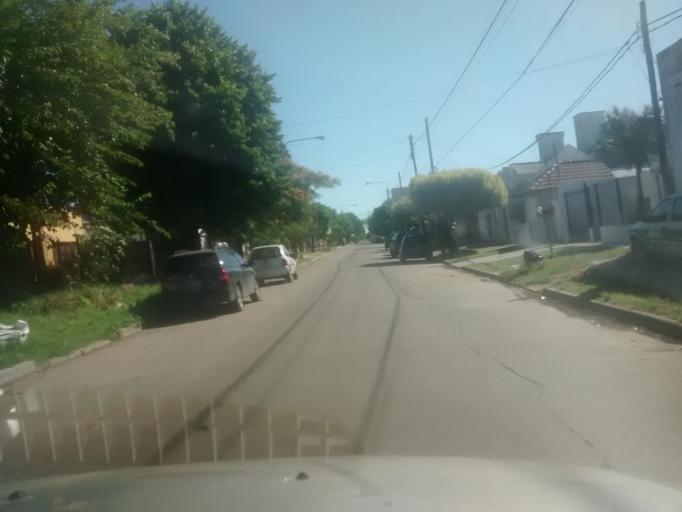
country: AR
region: Buenos Aires
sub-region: Partido de La Plata
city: La Plata
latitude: -34.9387
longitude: -57.9321
